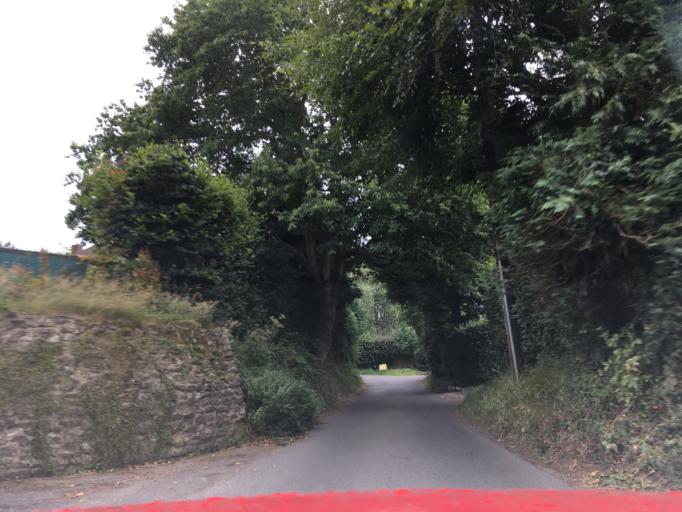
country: GB
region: England
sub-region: Kent
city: Maidstone
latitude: 51.2402
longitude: 0.4948
